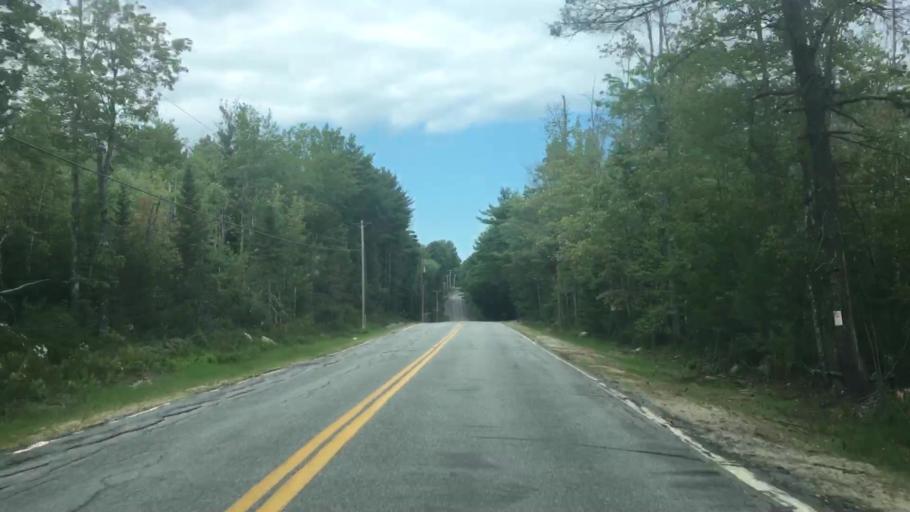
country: US
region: Maine
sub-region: Oxford County
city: Oxford
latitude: 44.0619
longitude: -70.5502
